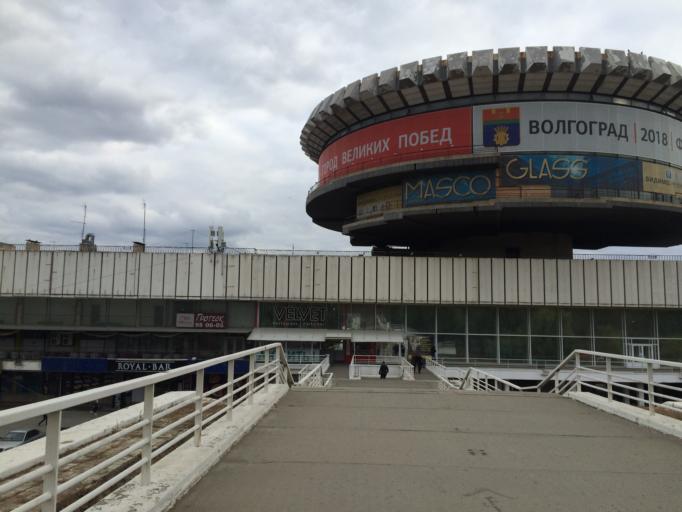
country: RU
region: Volgograd
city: Volgograd
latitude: 48.7016
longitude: 44.5189
